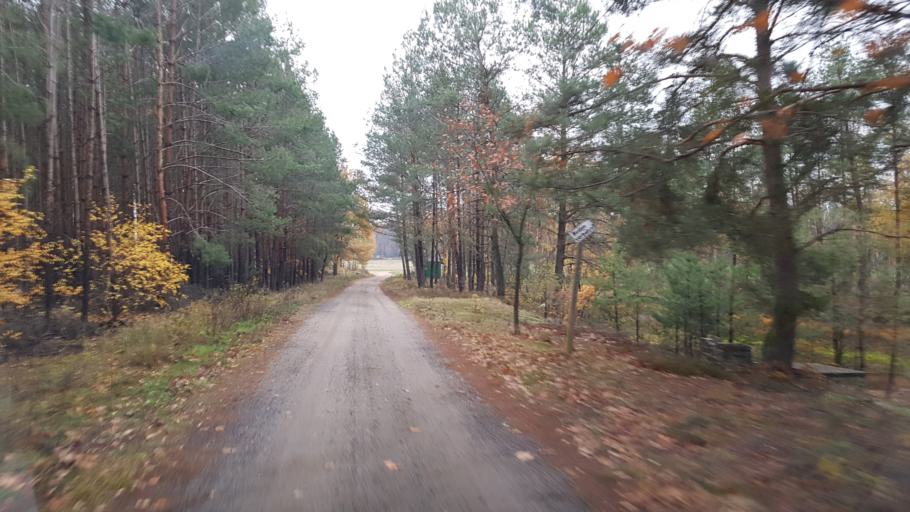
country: DE
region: Brandenburg
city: Schilda
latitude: 51.6401
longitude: 13.3970
